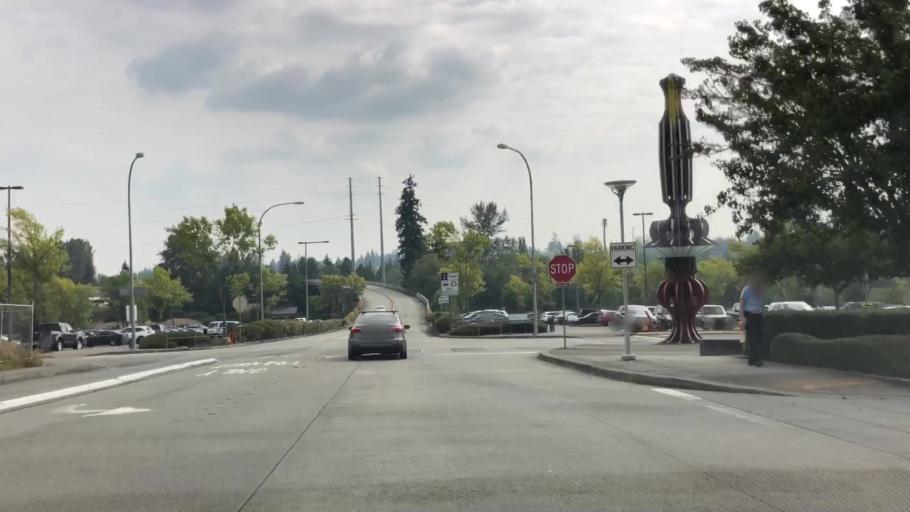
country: US
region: Washington
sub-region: Snohomish County
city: Alderwood Manor
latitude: 47.8161
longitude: -122.2950
